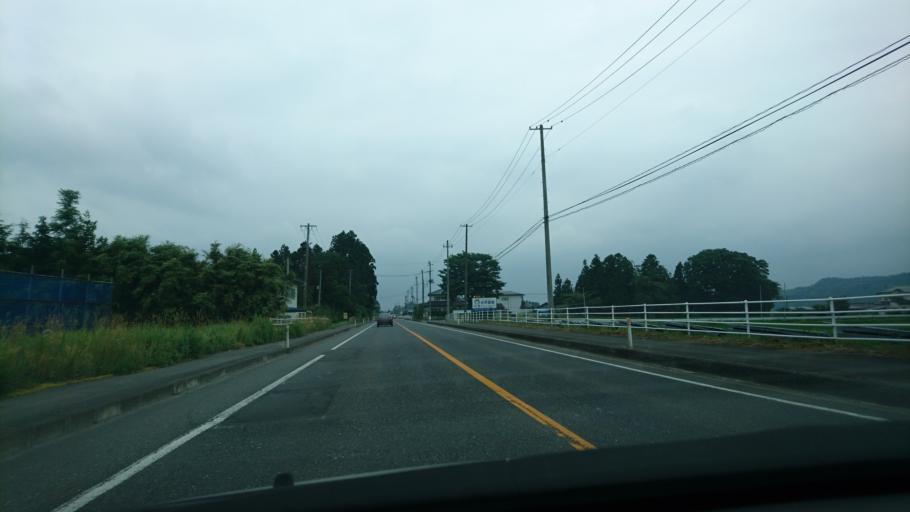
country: JP
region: Miyagi
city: Furukawa
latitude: 38.6877
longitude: 140.8519
